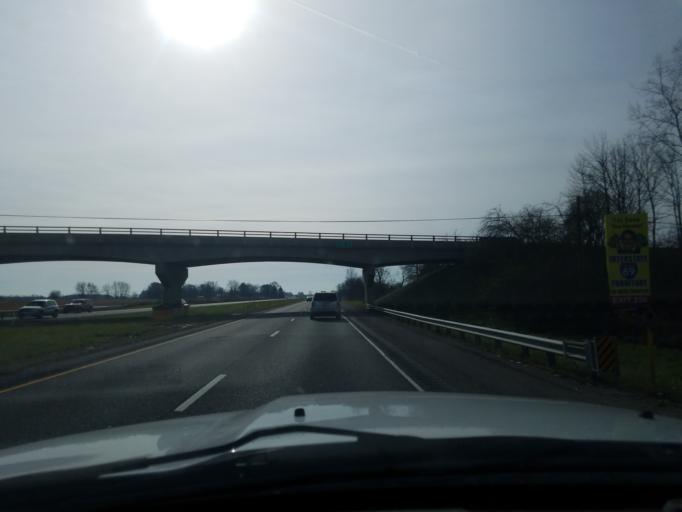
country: US
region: Indiana
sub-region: Delaware County
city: Daleville
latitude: 40.1791
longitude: -85.5640
